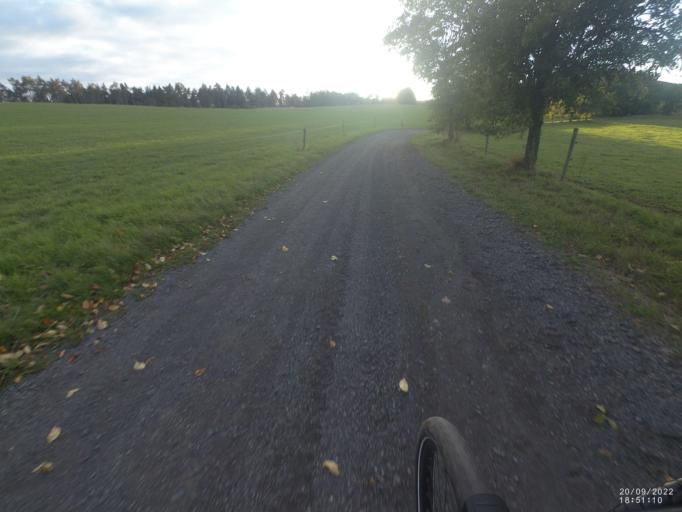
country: DE
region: Rheinland-Pfalz
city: Steiningen
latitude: 50.1748
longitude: 6.9323
